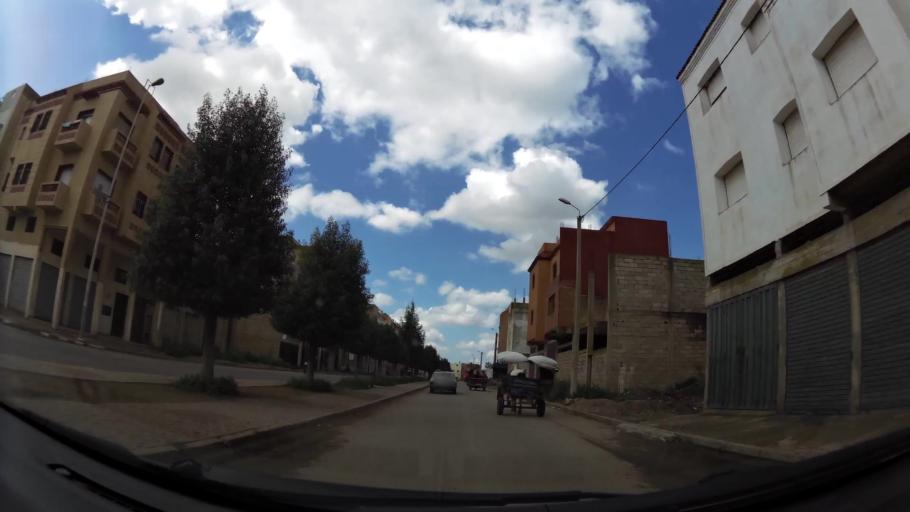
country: MA
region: Grand Casablanca
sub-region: Mediouna
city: Mediouna
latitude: 33.3706
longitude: -7.5303
